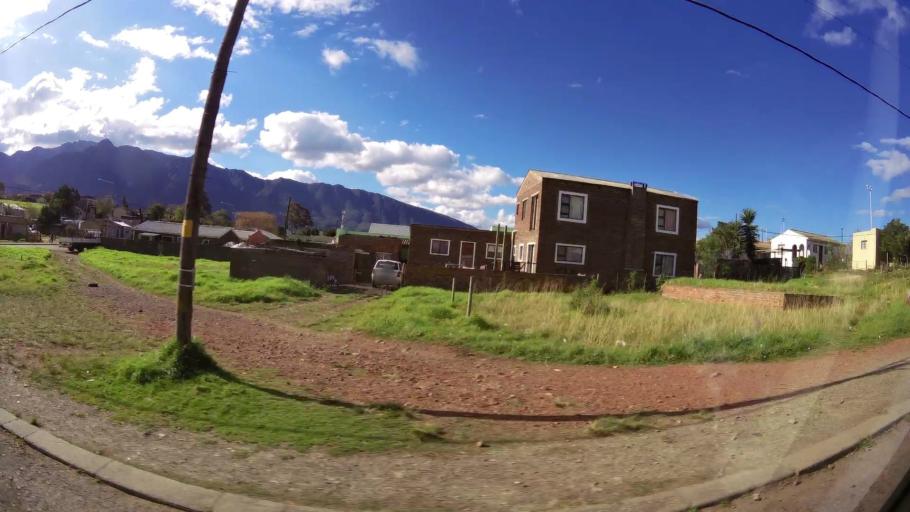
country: ZA
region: Western Cape
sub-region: Overberg District Municipality
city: Swellendam
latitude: -34.0385
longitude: 20.4419
